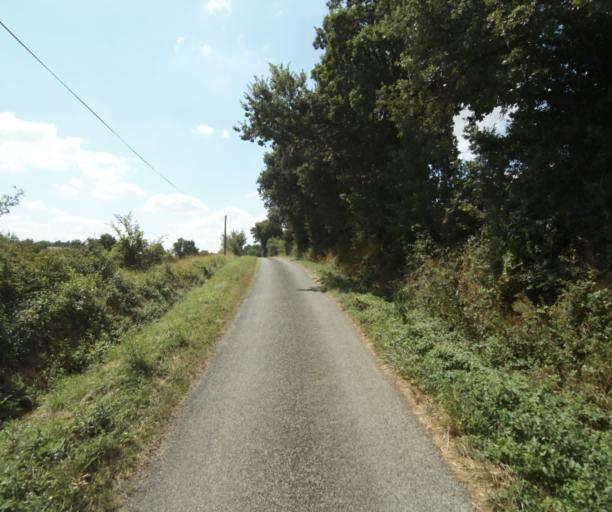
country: FR
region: Midi-Pyrenees
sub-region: Departement de la Haute-Garonne
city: Auriac-sur-Vendinelle
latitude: 43.4792
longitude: 1.7962
